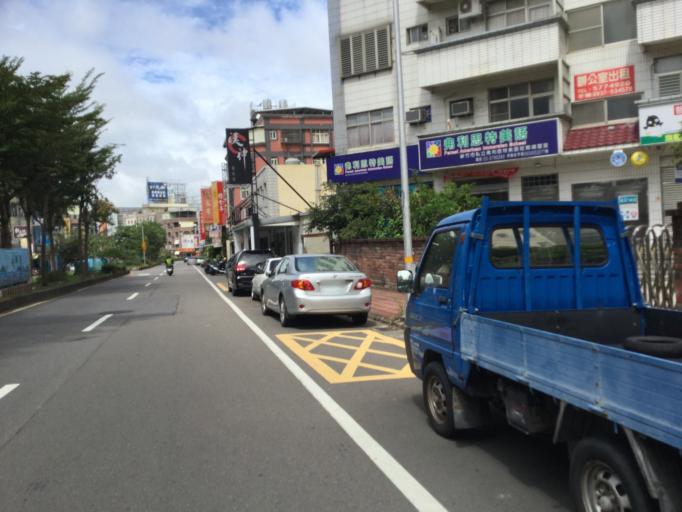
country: TW
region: Taiwan
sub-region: Hsinchu
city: Hsinchu
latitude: 24.7849
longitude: 121.0108
